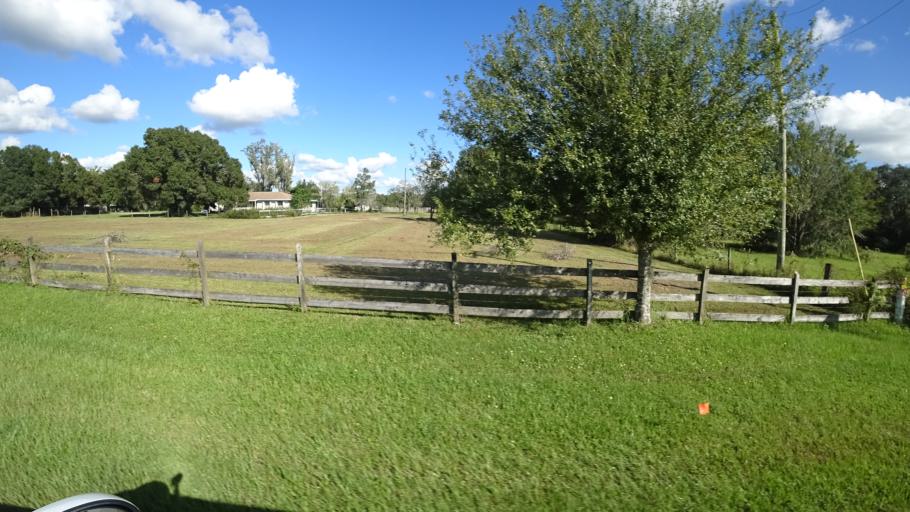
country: US
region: Florida
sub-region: Sarasota County
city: Lake Sarasota
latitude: 27.3350
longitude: -82.2694
